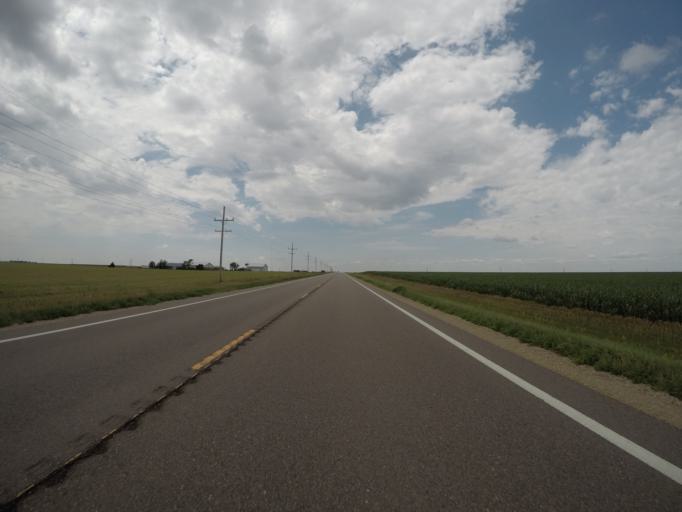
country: US
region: Kansas
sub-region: Thomas County
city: Colby
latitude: 39.3944
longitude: -100.9912
